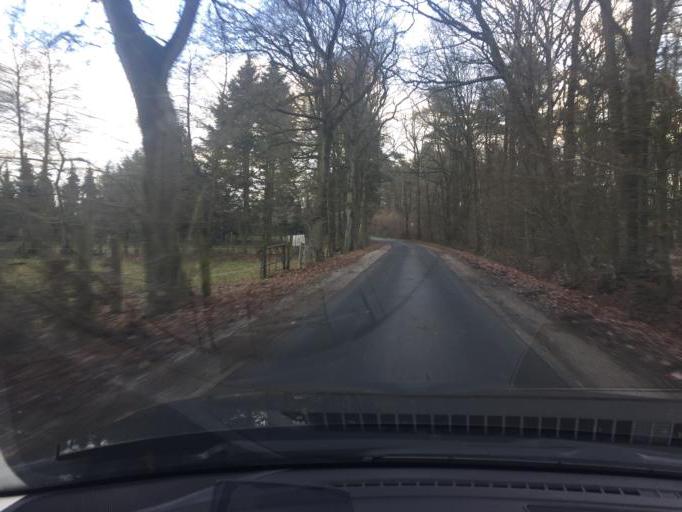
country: DE
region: North Rhine-Westphalia
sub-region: Regierungsbezirk Dusseldorf
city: Schermbeck
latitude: 51.6991
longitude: 6.8553
